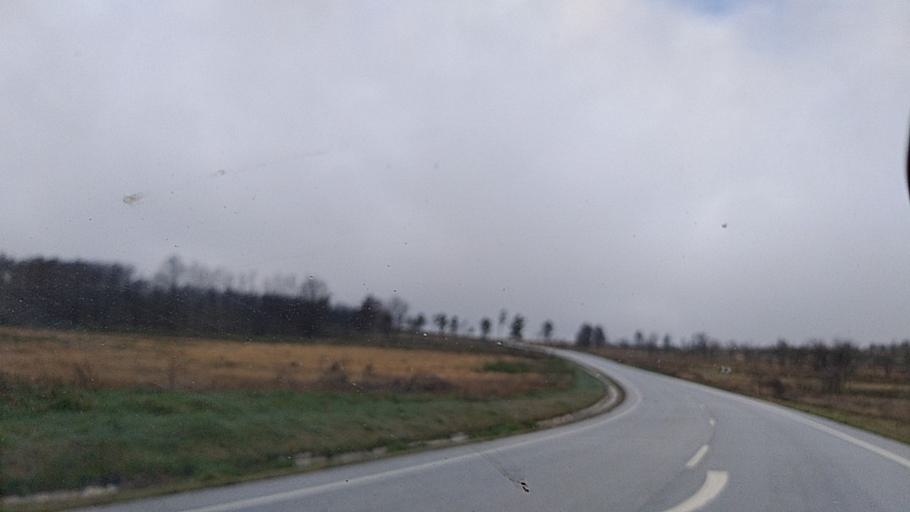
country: PT
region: Guarda
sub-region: Fornos de Algodres
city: Fornos de Algodres
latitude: 40.6981
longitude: -7.4743
